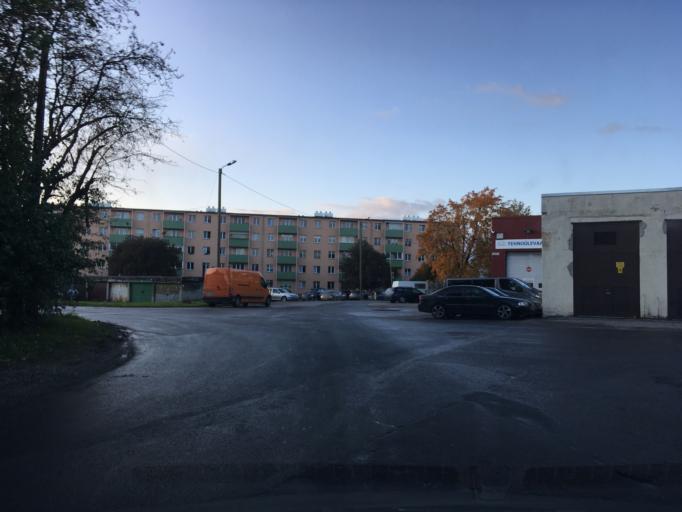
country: EE
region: Harju
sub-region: Tallinna linn
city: Tallinn
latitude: 59.4288
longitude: 24.8079
